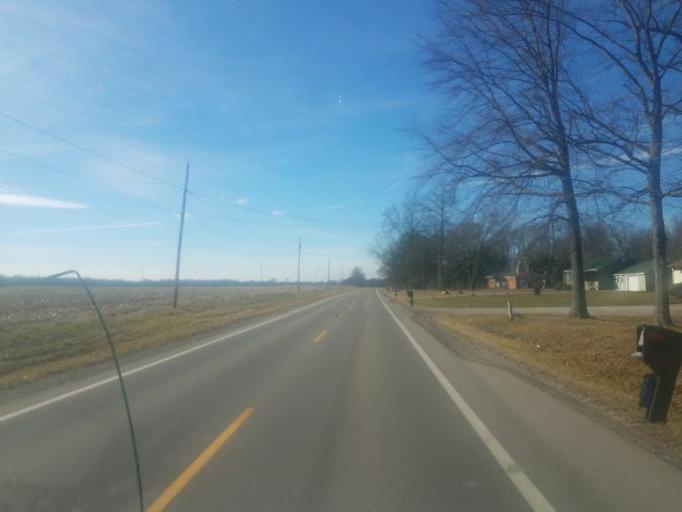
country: US
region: Ohio
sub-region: Crawford County
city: Galion
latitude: 40.6836
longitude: -82.7950
